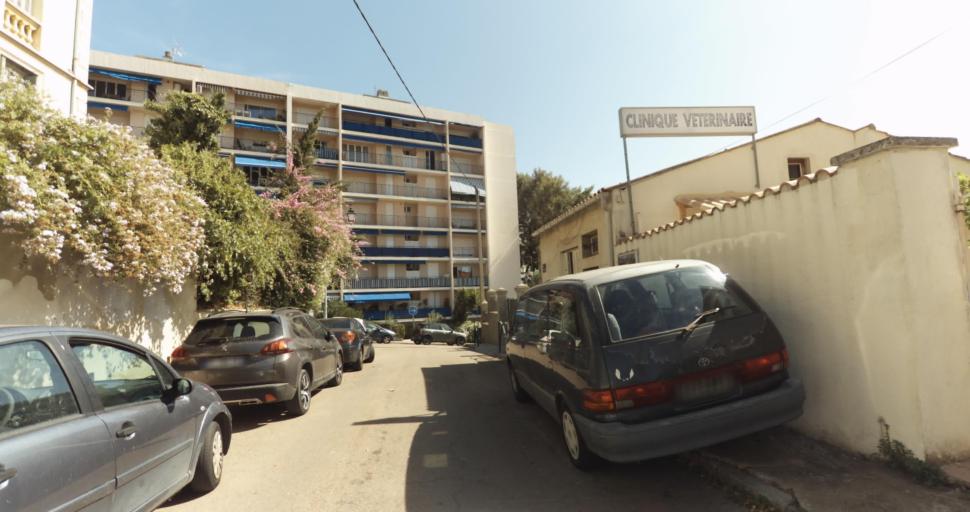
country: FR
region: Corsica
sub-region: Departement de la Corse-du-Sud
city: Ajaccio
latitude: 41.9155
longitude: 8.7266
